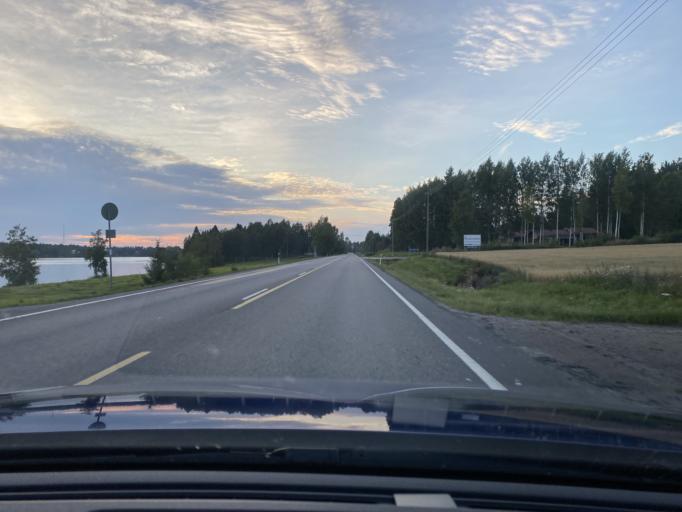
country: FI
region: Satakunta
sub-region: Pohjois-Satakunta
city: Kankaanpaeae
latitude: 61.7893
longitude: 22.4151
